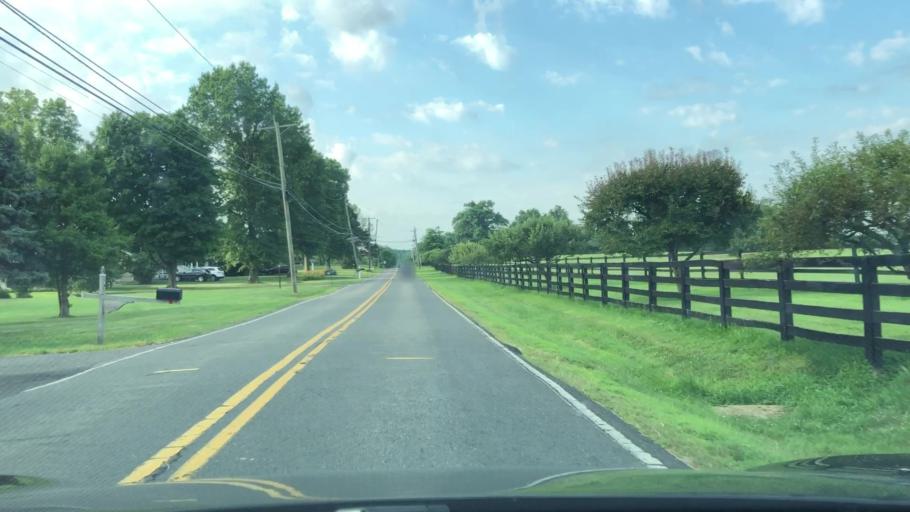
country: US
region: New Jersey
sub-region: Mercer County
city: Pennington
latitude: 40.3372
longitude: -74.8168
